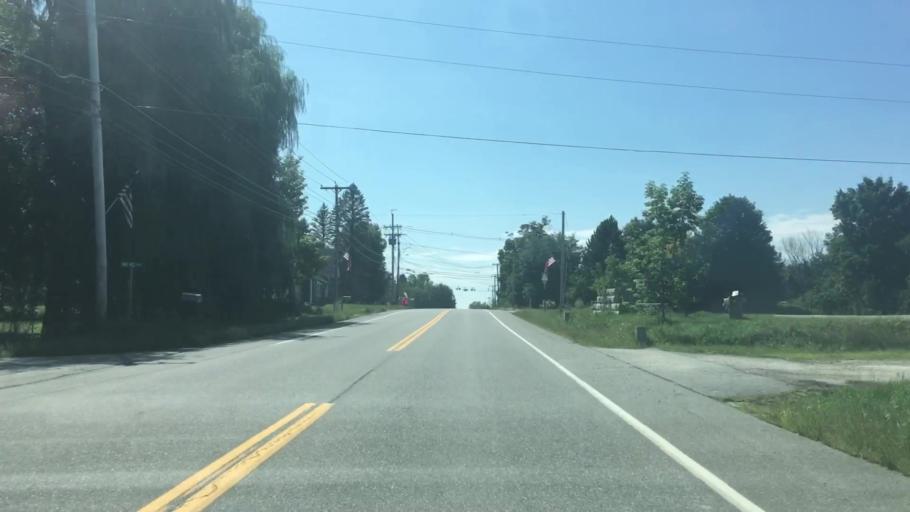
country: US
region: Maine
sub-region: Kennebec County
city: Monmouth
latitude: 44.1827
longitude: -69.9908
